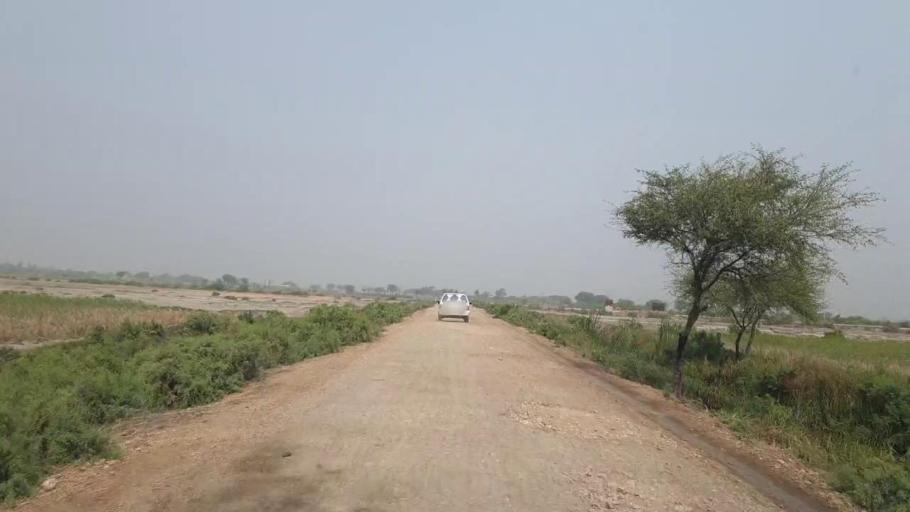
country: PK
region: Sindh
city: Kario
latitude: 24.6557
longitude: 68.6584
